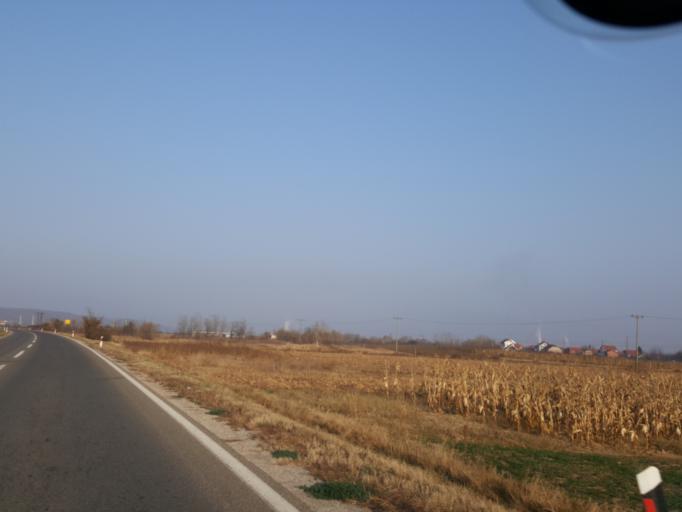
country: RS
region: Central Serbia
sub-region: Jablanicki Okrug
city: Leskovac
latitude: 42.9346
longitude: 22.0105
